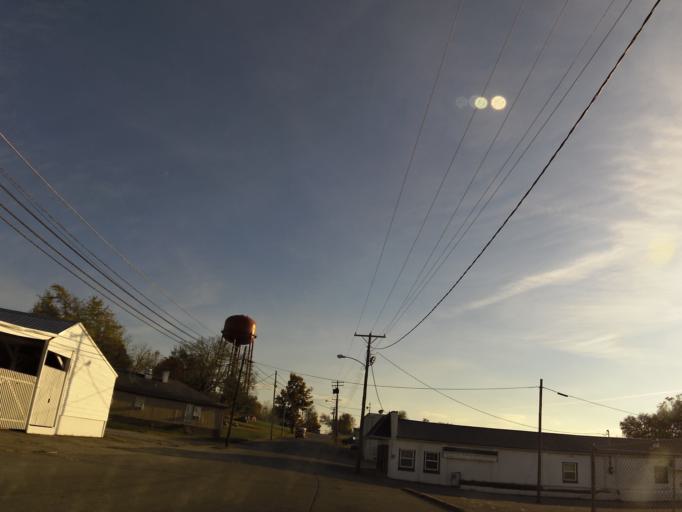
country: US
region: Kentucky
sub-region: Garrard County
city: Lancaster
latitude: 37.6176
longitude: -84.5774
